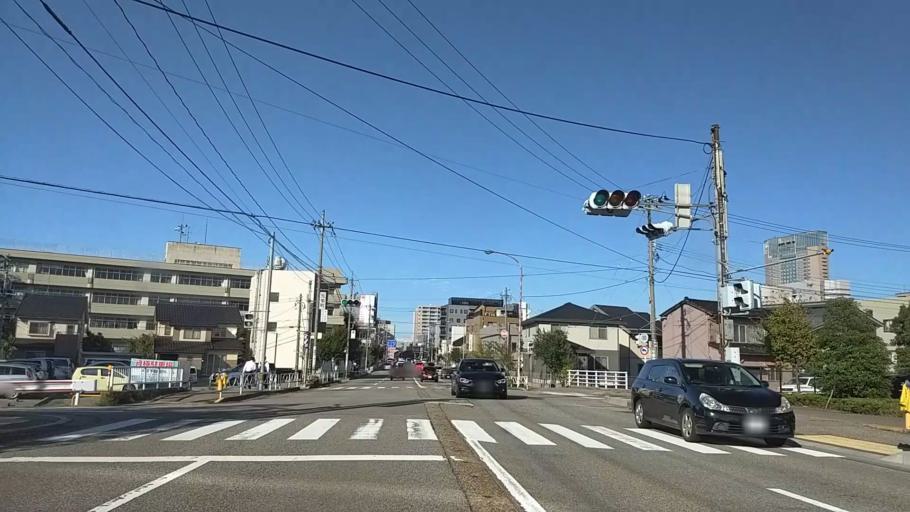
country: JP
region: Ishikawa
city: Kanazawa-shi
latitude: 36.5741
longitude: 136.6415
